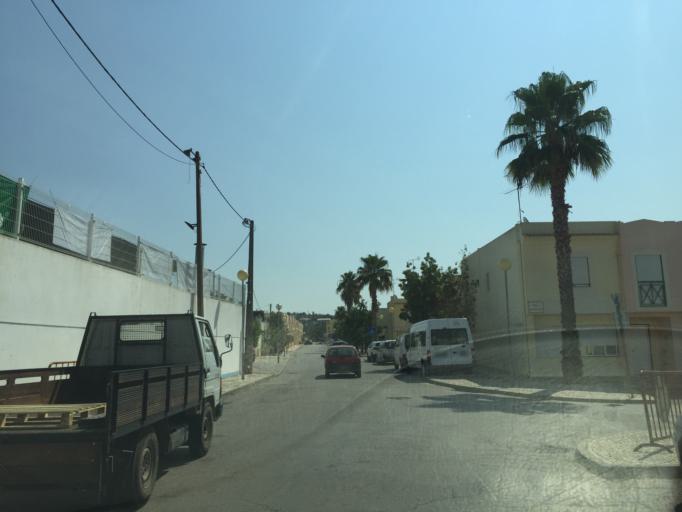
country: PT
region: Faro
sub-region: Faro
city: Faro
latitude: 37.0613
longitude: -7.9176
